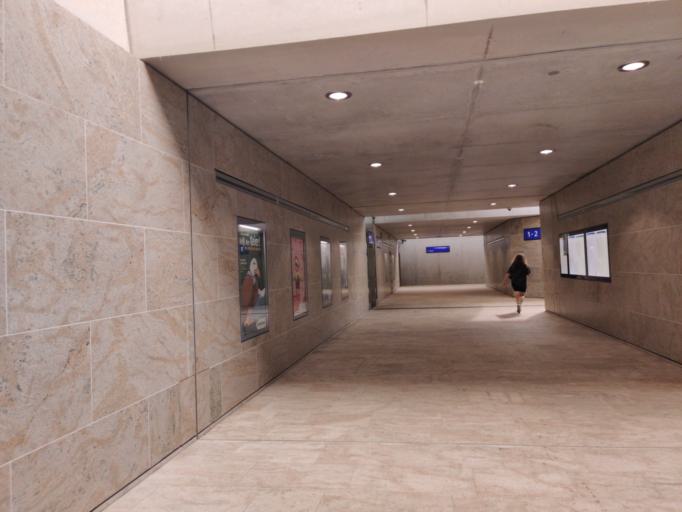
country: AT
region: Vorarlberg
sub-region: Politischer Bezirk Dornbirn
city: Lustenau
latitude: 47.4509
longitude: 9.6671
